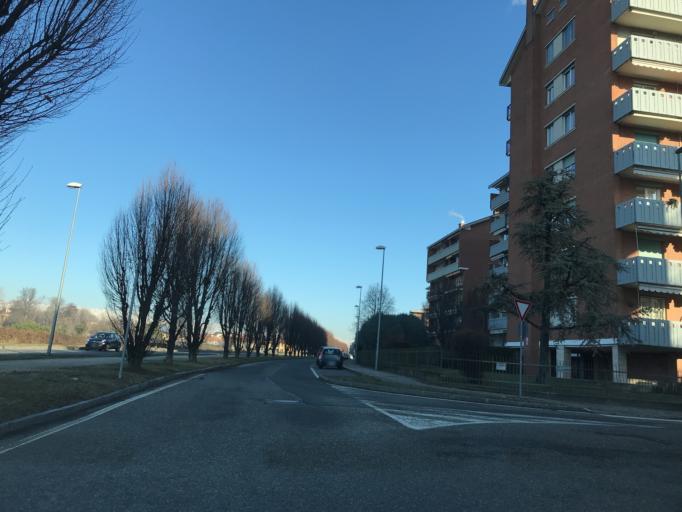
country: IT
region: Piedmont
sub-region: Provincia di Torino
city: Gerbido
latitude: 45.0414
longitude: 7.6152
